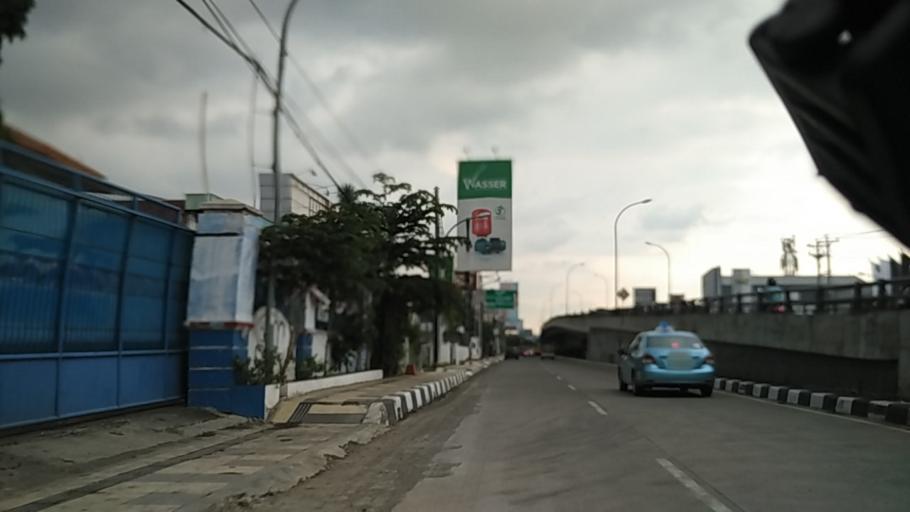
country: ID
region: Central Java
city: Semarang
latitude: -6.9842
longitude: 110.3865
